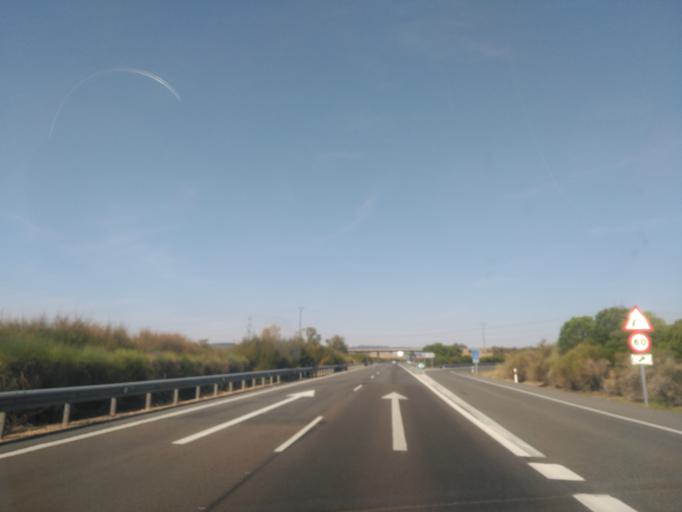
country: ES
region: Castille and Leon
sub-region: Provincia de Valladolid
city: Tordesillas
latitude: 41.5010
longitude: -5.0214
